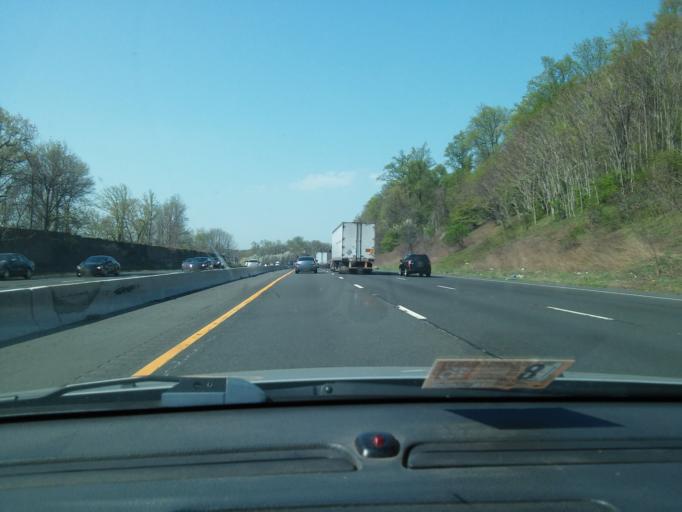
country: US
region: New Jersey
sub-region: Union County
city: Scotch Plains
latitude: 40.6705
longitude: -74.4094
